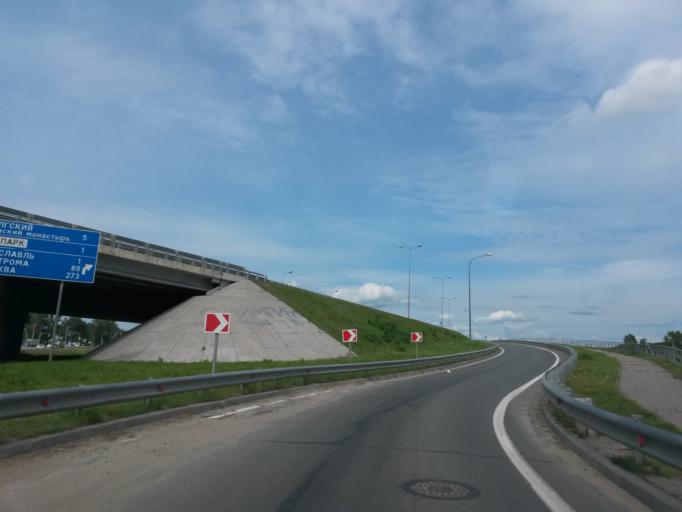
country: RU
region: Jaroslavl
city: Yaroslavl
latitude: 57.6865
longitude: 39.9025
